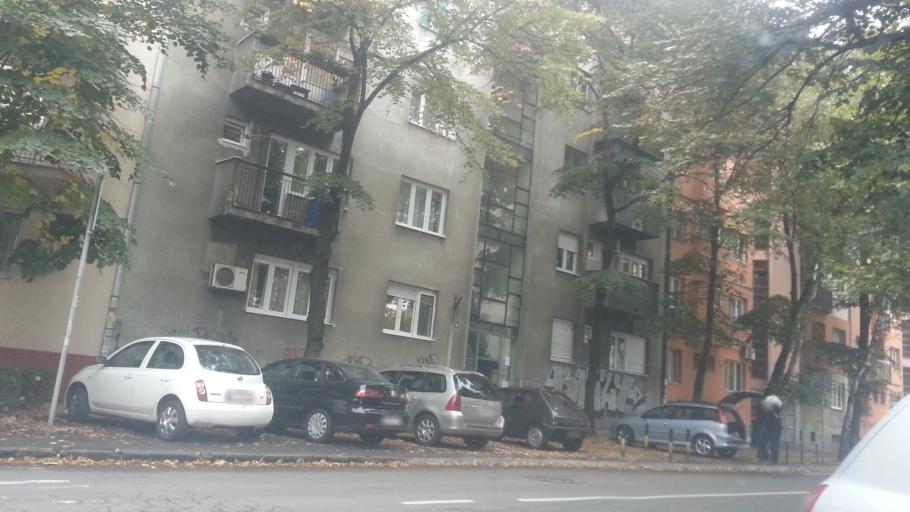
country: RS
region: Central Serbia
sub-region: Belgrade
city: Zemun
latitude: 44.8406
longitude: 20.3936
